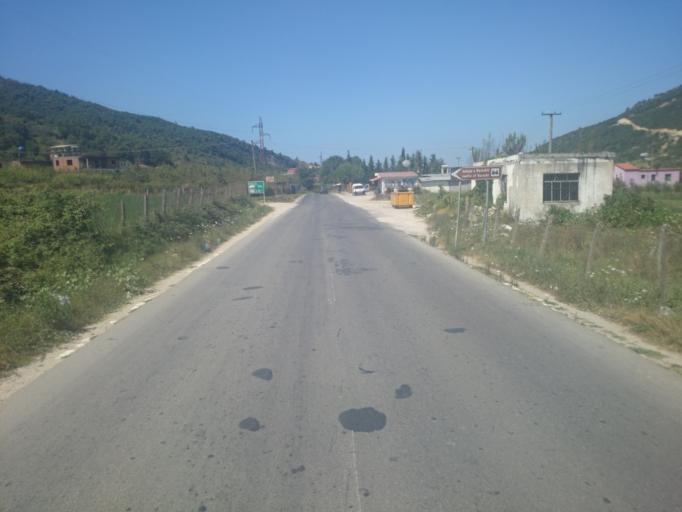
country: AL
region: Tirane
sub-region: Rrethi i Tiranes
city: Ndroq
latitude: 41.2608
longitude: 19.6729
